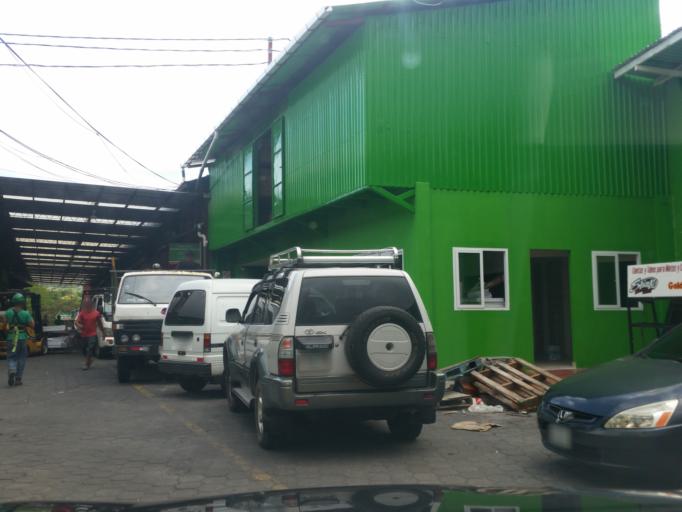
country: NI
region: Managua
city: Managua
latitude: 12.1247
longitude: -86.2819
